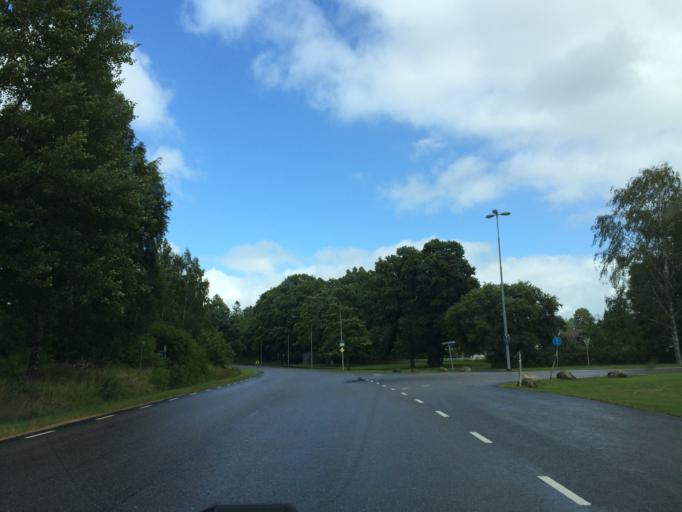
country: SE
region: Vaestra Goetaland
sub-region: Trollhattan
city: Trollhattan
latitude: 58.2783
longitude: 12.2645
